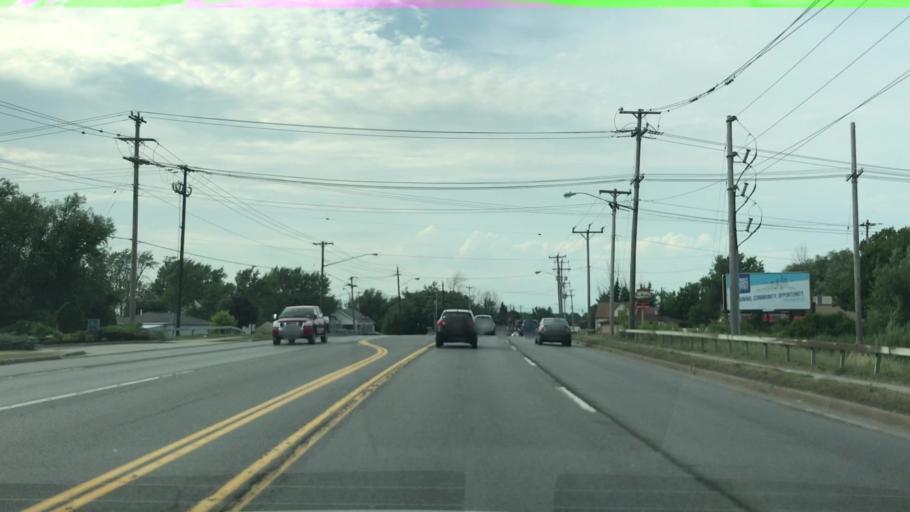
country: US
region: New York
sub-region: Erie County
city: Cheektowaga
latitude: 42.9241
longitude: -78.7415
